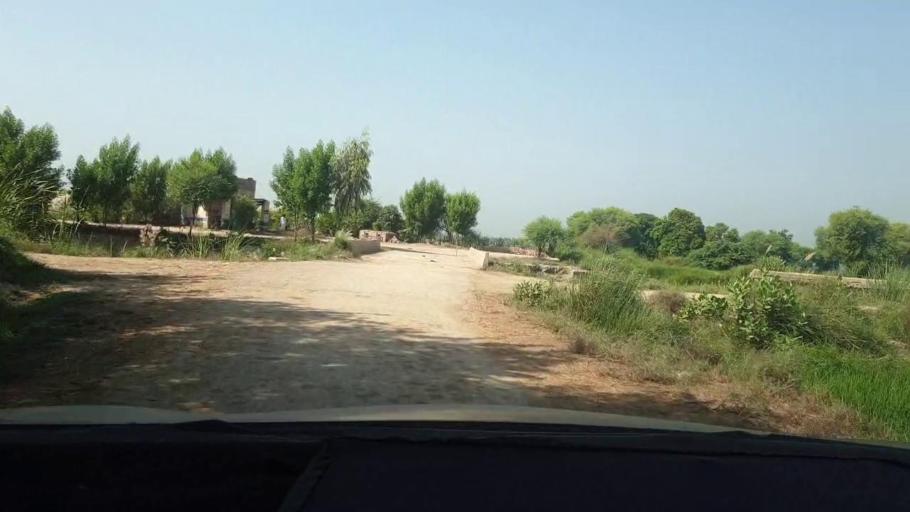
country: PK
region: Sindh
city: Miro Khan
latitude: 27.7029
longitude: 68.0883
